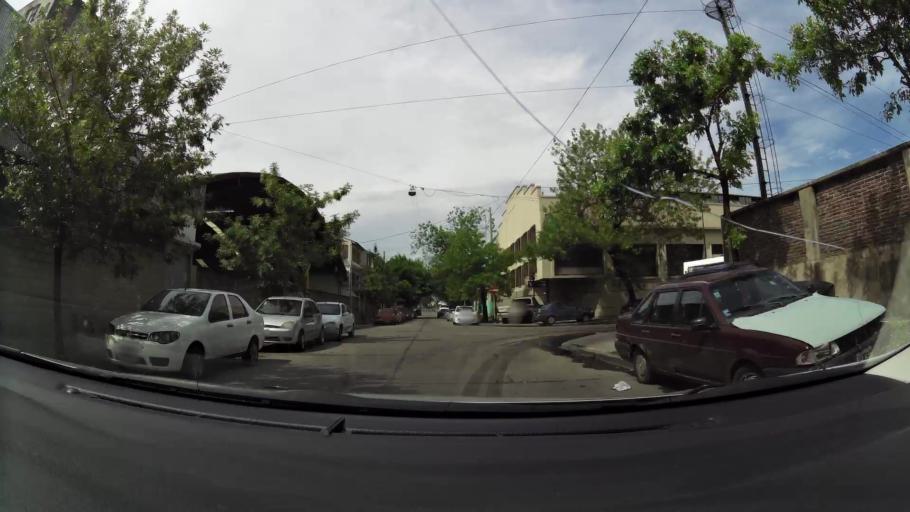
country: AR
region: Buenos Aires
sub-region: Partido de Lanus
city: Lanus
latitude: -34.6576
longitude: -58.4180
